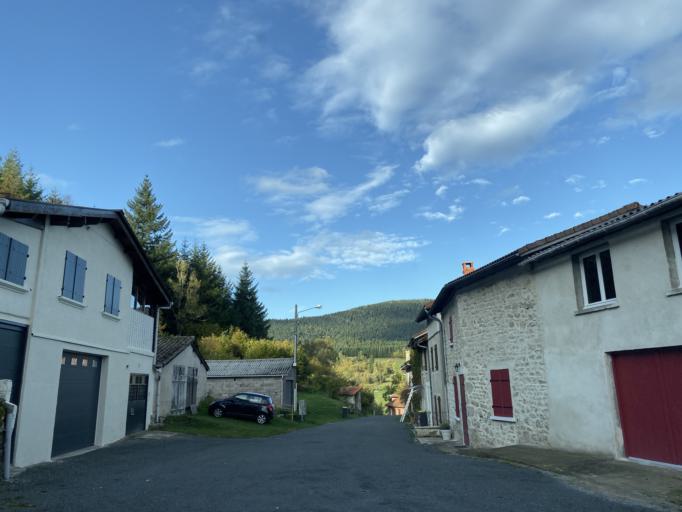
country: FR
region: Auvergne
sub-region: Departement du Puy-de-Dome
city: Celles-sur-Durolle
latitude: 45.7830
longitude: 3.6628
